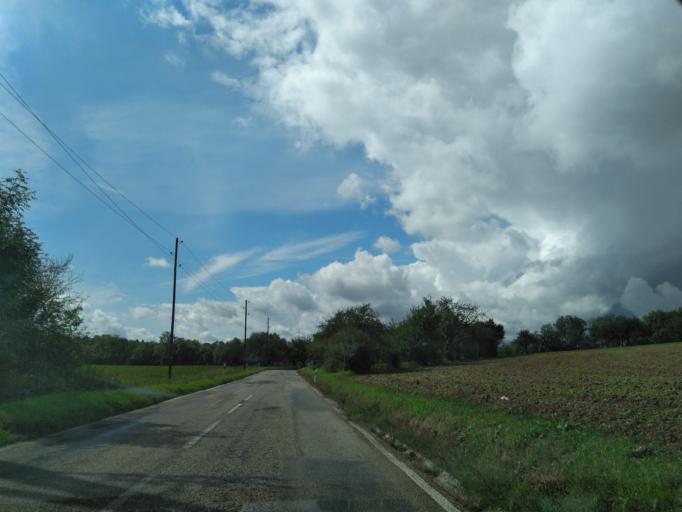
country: DE
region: Baden-Wuerttemberg
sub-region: Regierungsbezirk Stuttgart
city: Markgroningen
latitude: 48.9370
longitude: 9.0754
